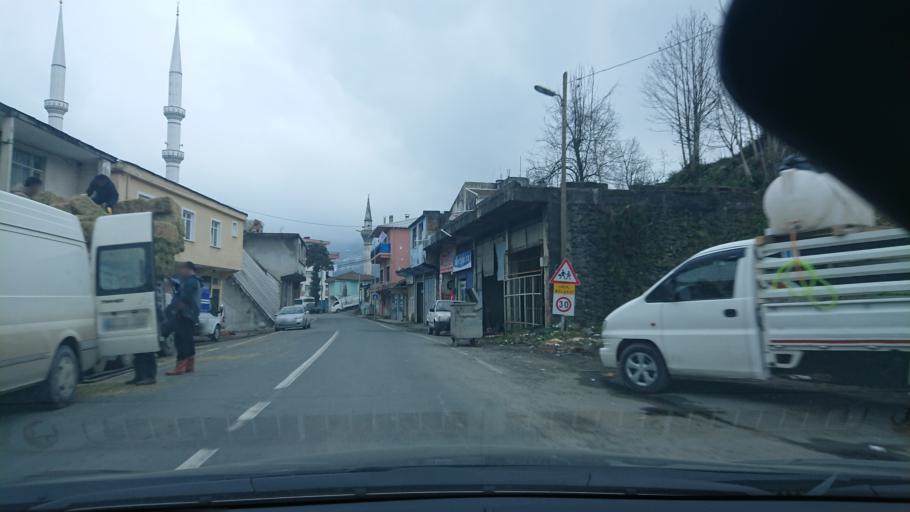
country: TR
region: Rize
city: Rize
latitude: 41.0000
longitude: 40.4875
